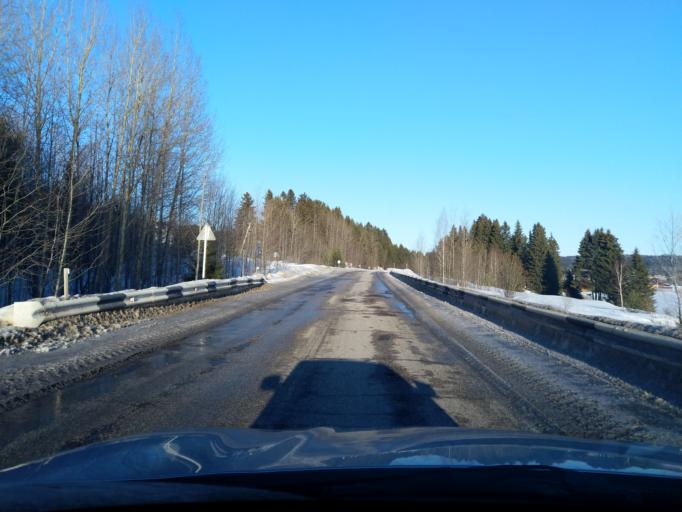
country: RU
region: Perm
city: Polazna
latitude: 58.3051
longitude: 56.4371
